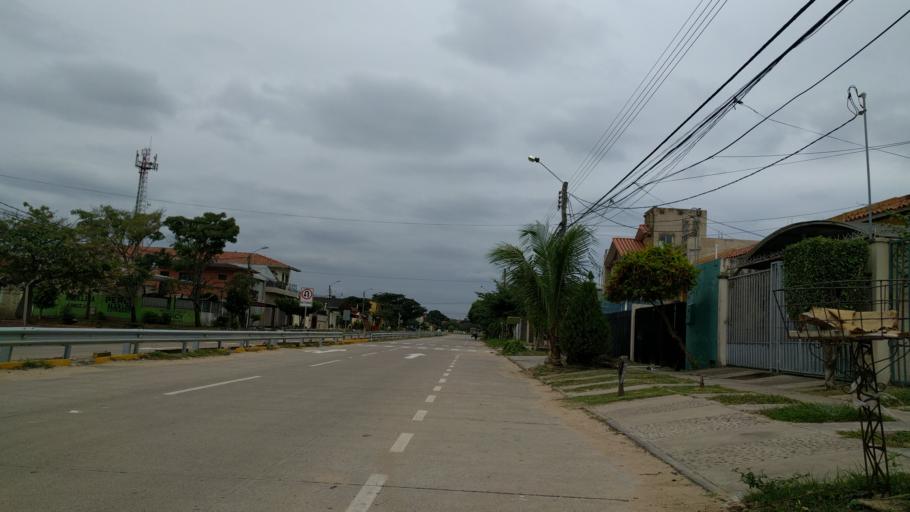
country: BO
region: Santa Cruz
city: Santa Cruz de la Sierra
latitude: -17.8019
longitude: -63.2162
